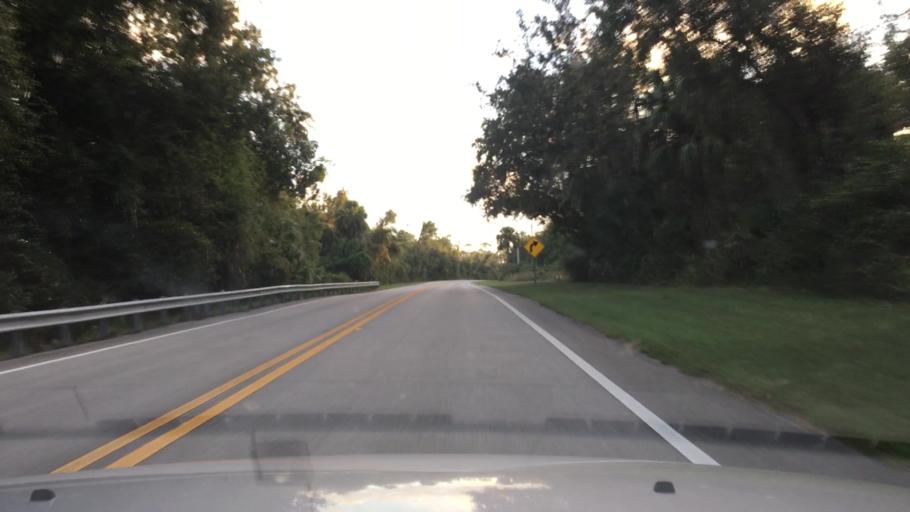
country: US
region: Florida
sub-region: Volusia County
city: Ormond Beach
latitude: 29.2948
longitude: -81.1079
